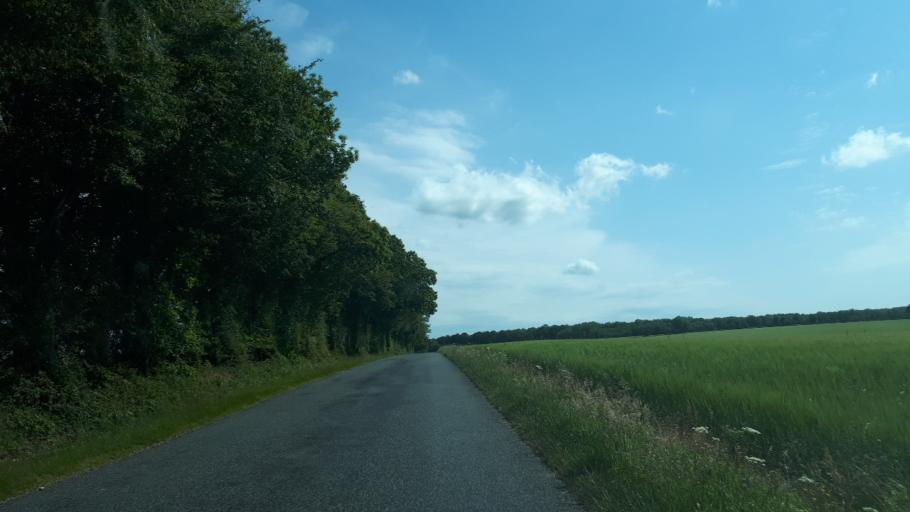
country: FR
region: Centre
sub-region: Departement du Cher
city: Blancafort
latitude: 47.4196
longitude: 2.6074
